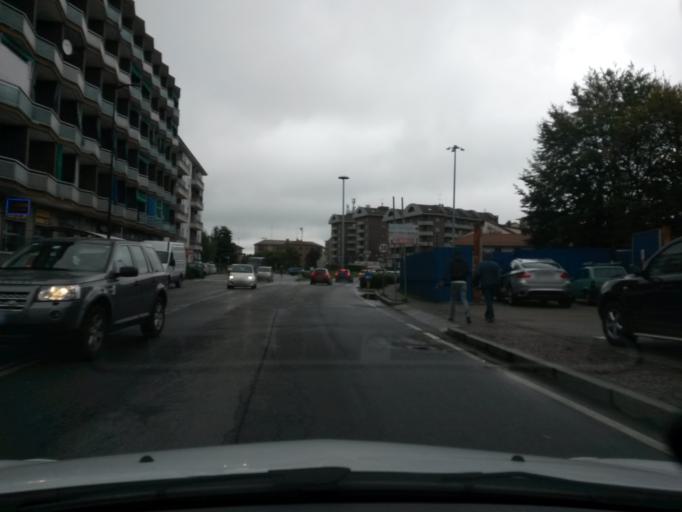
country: IT
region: Piedmont
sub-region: Provincia di Torino
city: Rivoli
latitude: 45.0763
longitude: 7.5185
